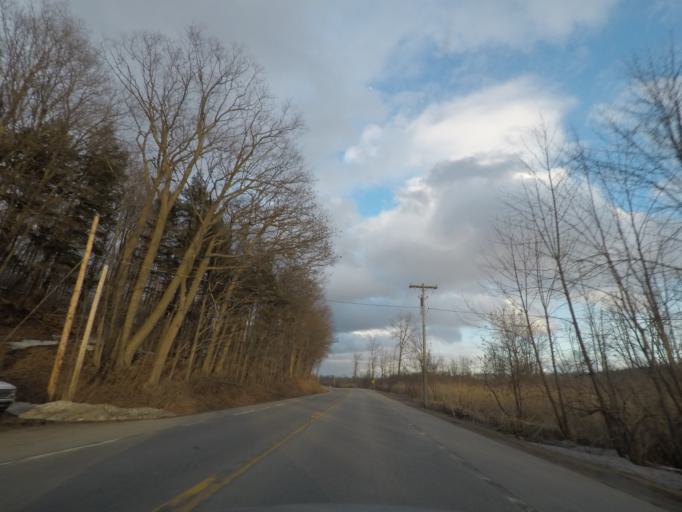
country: US
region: New York
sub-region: Montgomery County
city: Saint Johnsville
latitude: 43.0069
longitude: -74.7514
